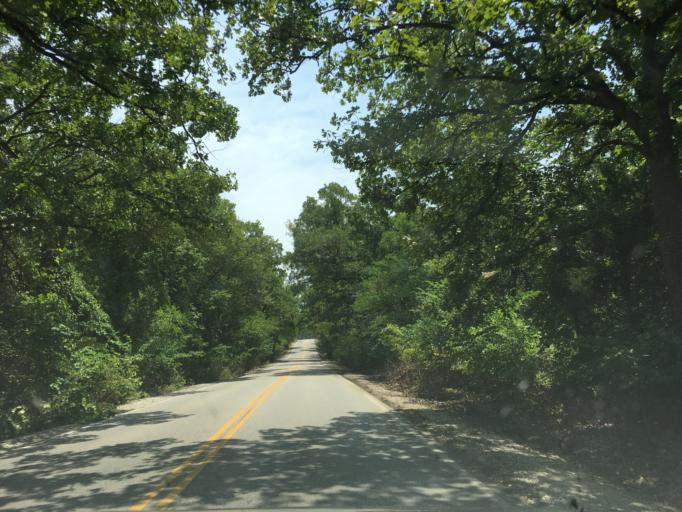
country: US
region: Oklahoma
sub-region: Tulsa County
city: Jenks
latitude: 36.0734
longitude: -95.9979
